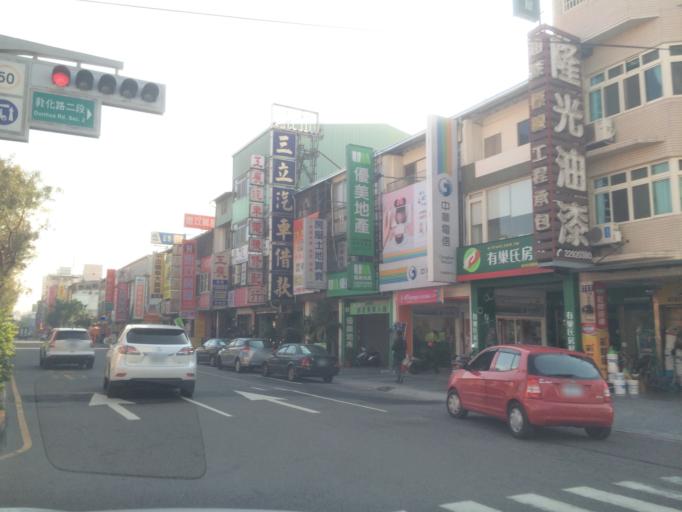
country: TW
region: Taiwan
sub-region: Taichung City
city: Taichung
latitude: 24.1856
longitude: 120.6641
